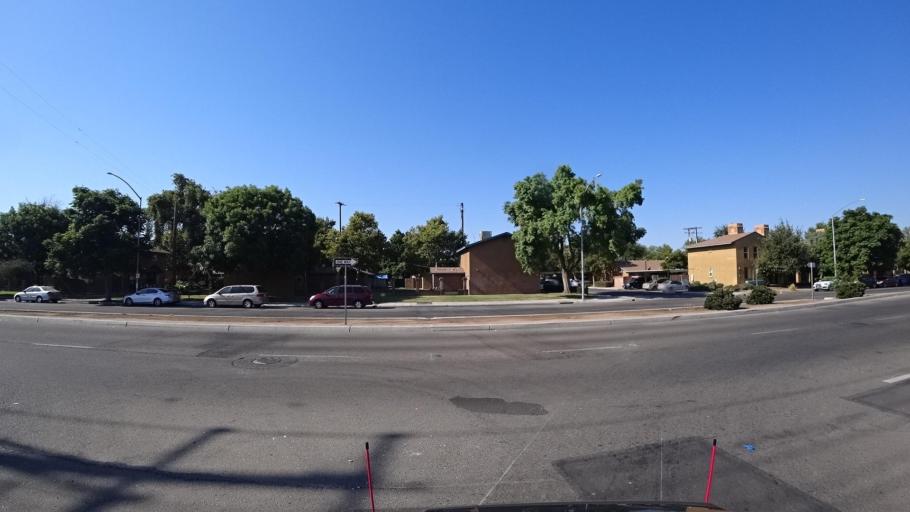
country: US
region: California
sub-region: Fresno County
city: West Park
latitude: 36.7215
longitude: -119.8222
